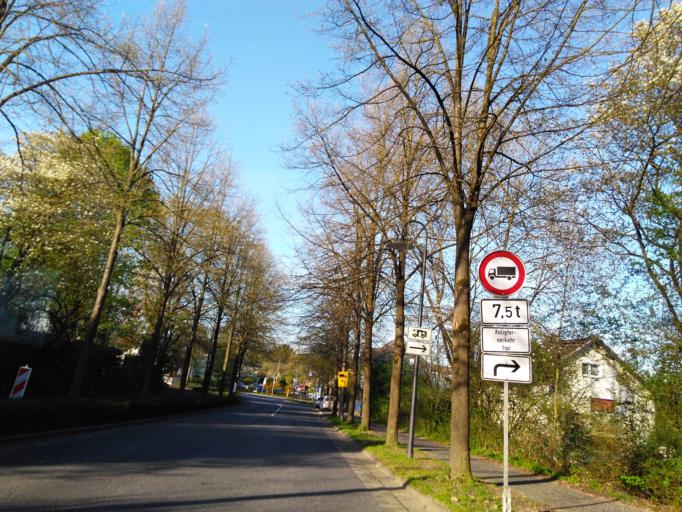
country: DE
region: North Rhine-Westphalia
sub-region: Regierungsbezirk Koln
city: Much
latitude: 50.9048
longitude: 7.3982
